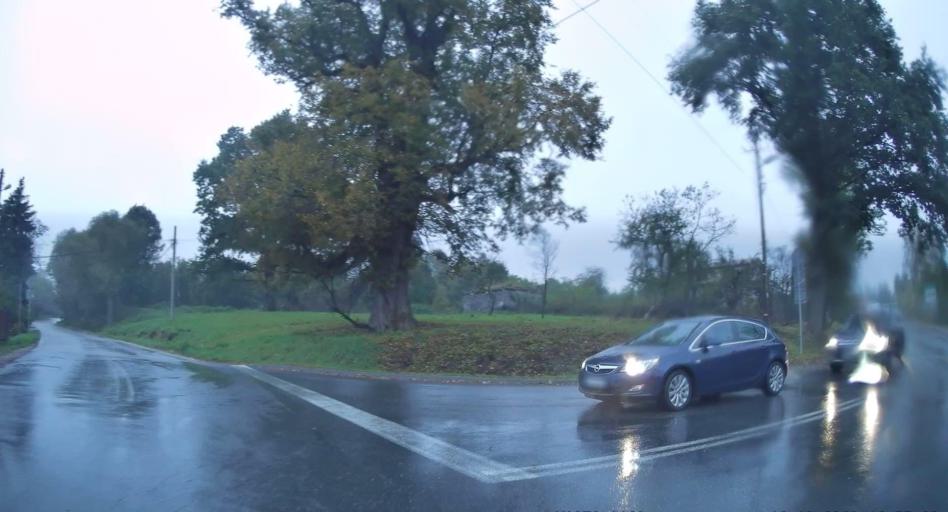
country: PL
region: Lesser Poland Voivodeship
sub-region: Powiat krakowski
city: Ochojno
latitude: 49.9731
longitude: 19.9875
